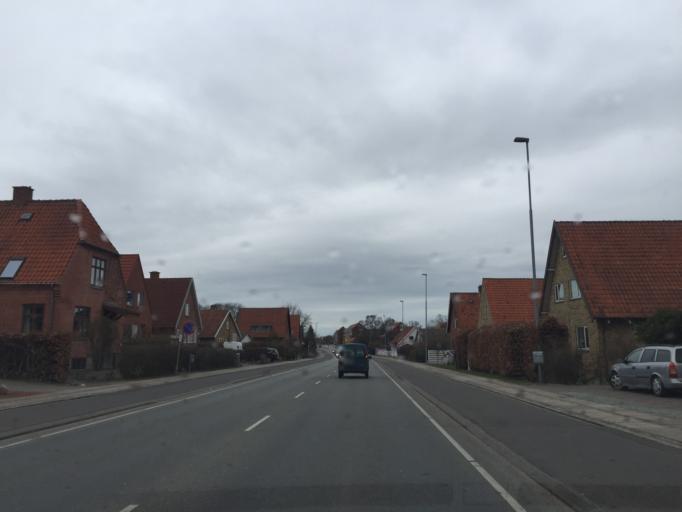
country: DK
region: South Denmark
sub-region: Odense Kommune
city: Odense
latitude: 55.3955
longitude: 10.3393
